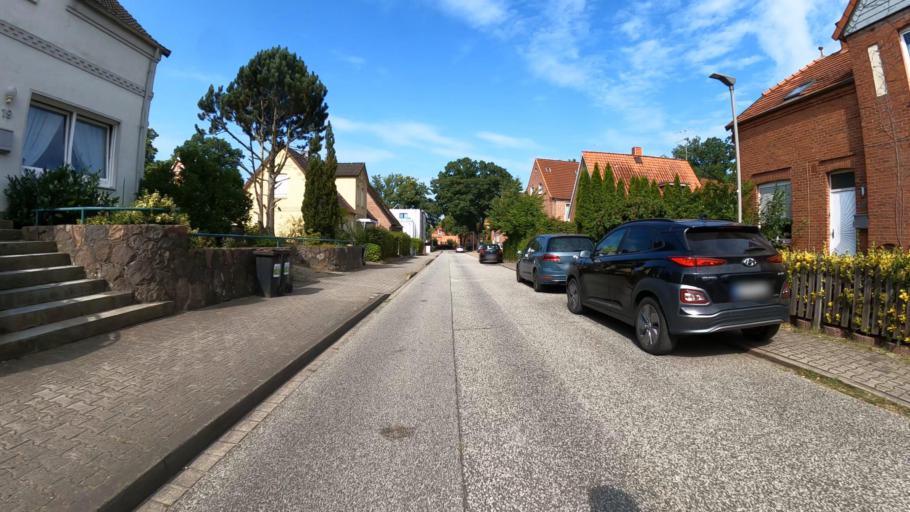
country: DE
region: Schleswig-Holstein
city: Geesthacht
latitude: 53.4313
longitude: 10.3825
